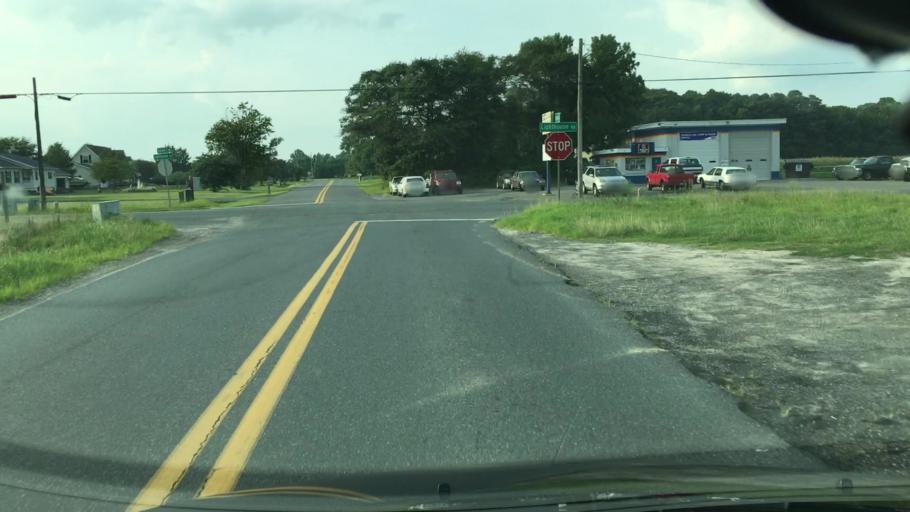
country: US
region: Delaware
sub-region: Sussex County
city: Selbyville
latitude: 38.4637
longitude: -75.1783
